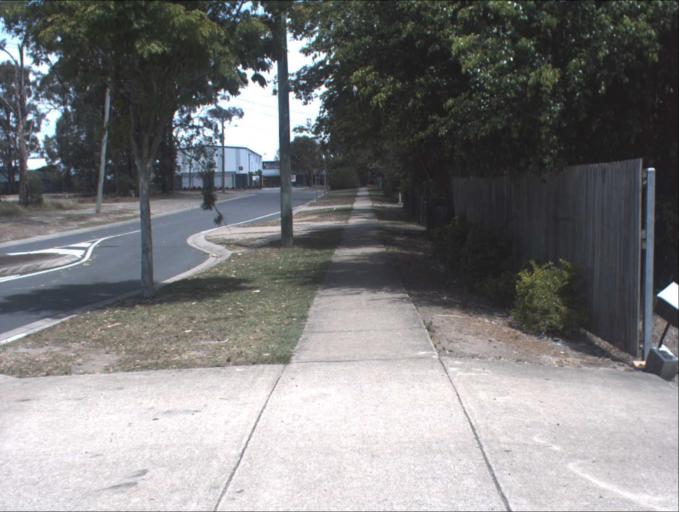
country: AU
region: Queensland
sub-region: Logan
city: Woodridge
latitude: -27.6408
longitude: 153.0973
